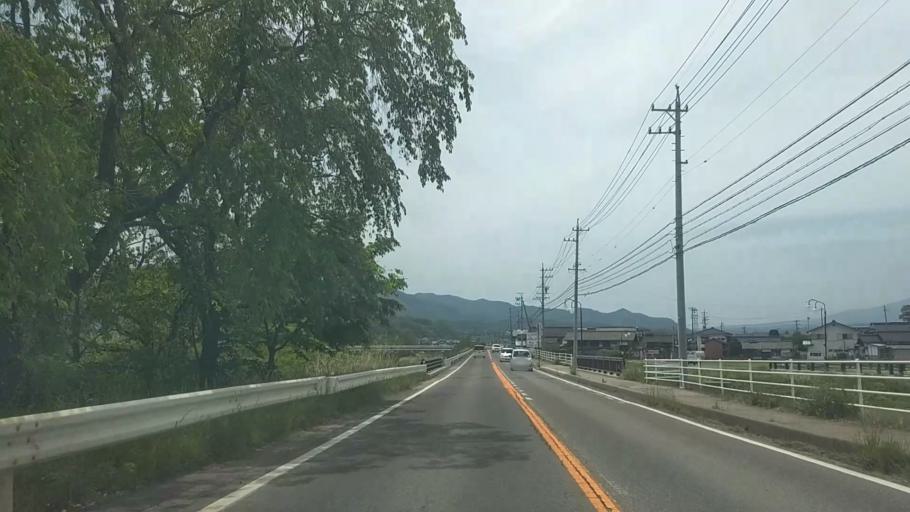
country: JP
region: Nagano
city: Saku
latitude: 36.1709
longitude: 138.4858
